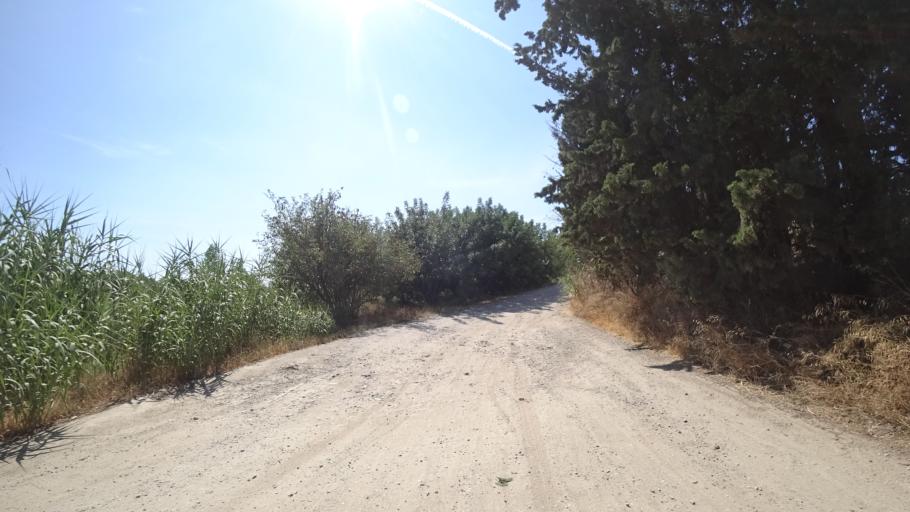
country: FR
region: Languedoc-Roussillon
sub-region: Departement des Pyrenees-Orientales
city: Rivesaltes
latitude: 42.7735
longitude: 2.8671
